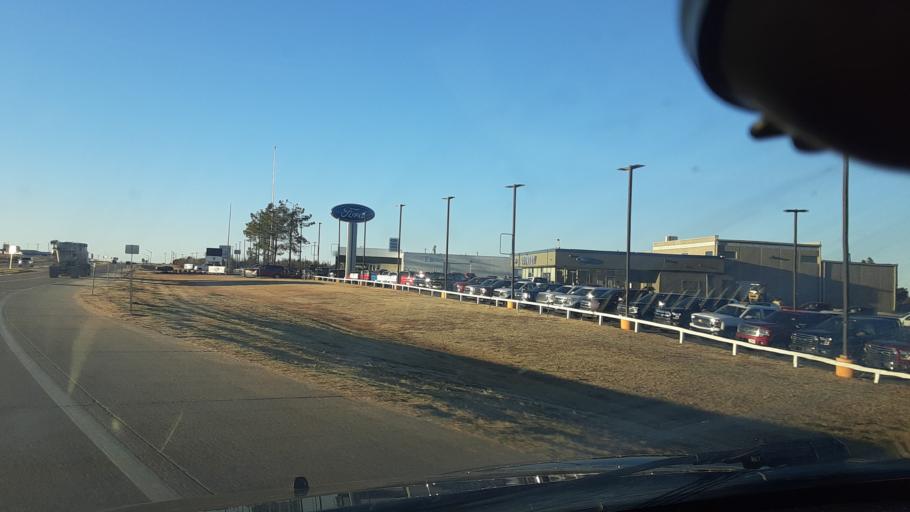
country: US
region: Oklahoma
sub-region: Logan County
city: Guthrie
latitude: 35.8220
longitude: -97.4170
